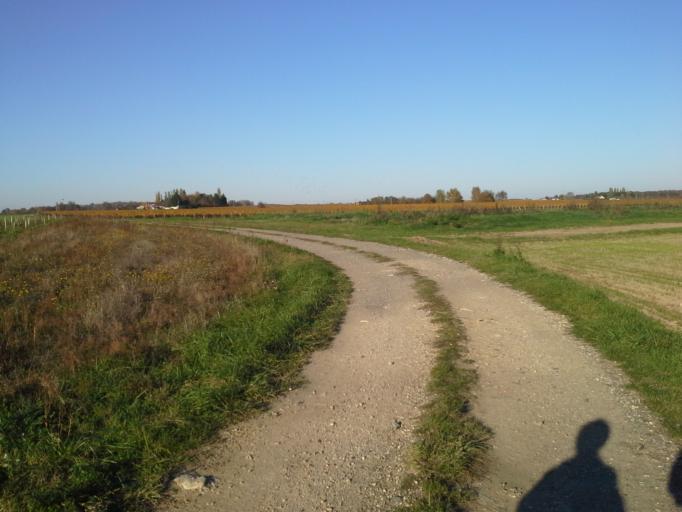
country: FR
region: Centre
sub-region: Departement du Loir-et-Cher
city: Saint-Romain-sur-Cher
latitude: 47.3662
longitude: 1.3974
